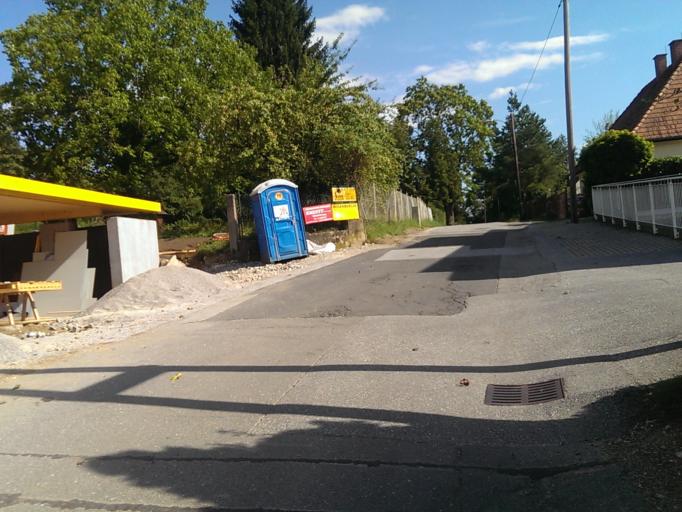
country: AT
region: Styria
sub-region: Graz Stadt
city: Graz
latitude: 47.0658
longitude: 15.4717
